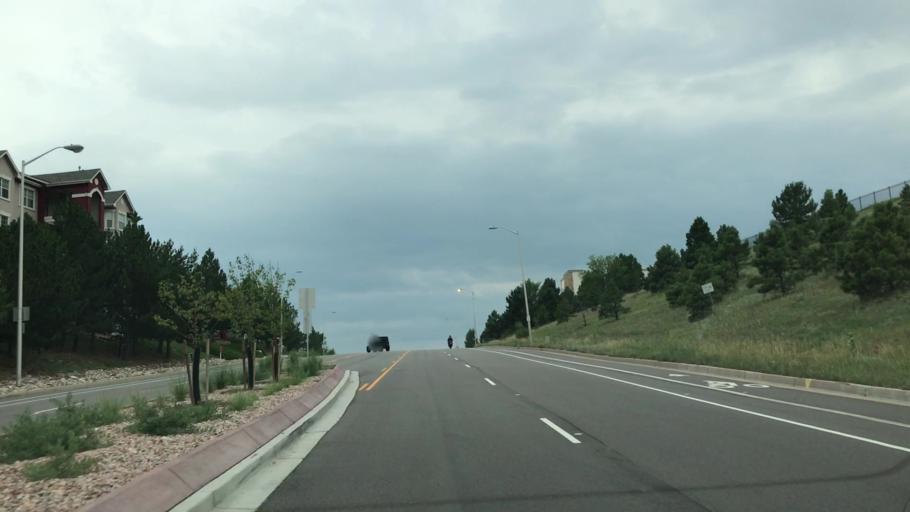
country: US
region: Colorado
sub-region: El Paso County
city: Colorado Springs
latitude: 38.8835
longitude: -104.8477
